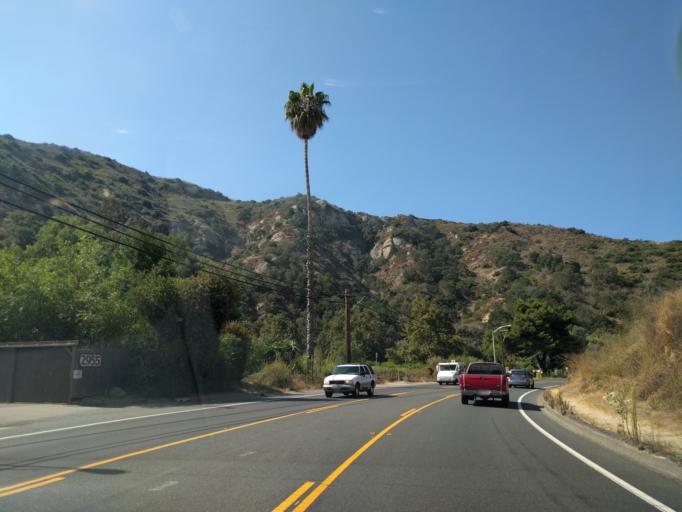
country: US
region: California
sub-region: Orange County
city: Laguna Beach
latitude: 33.5637
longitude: -117.7642
